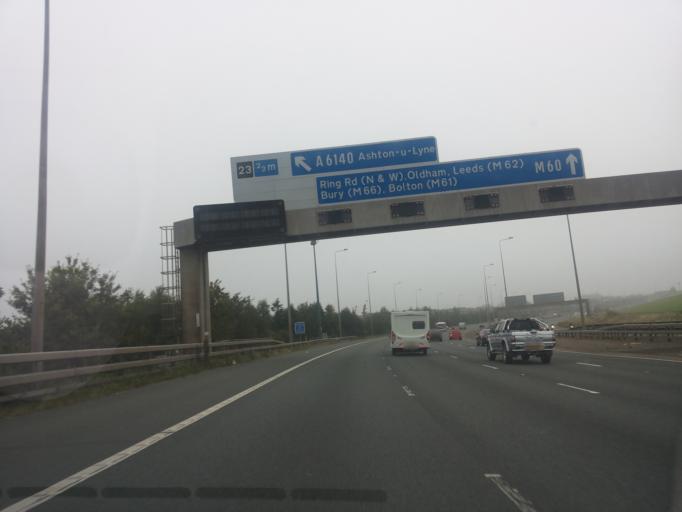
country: GB
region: England
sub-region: Borough of Tameside
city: Droylsden
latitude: 53.4675
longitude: -2.1395
